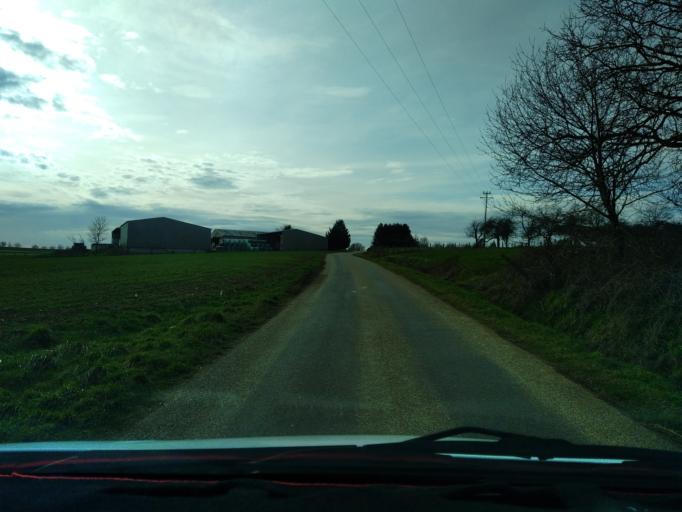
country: FR
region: Franche-Comte
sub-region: Departement de la Haute-Saone
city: Marnay
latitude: 47.3618
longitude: 5.6822
